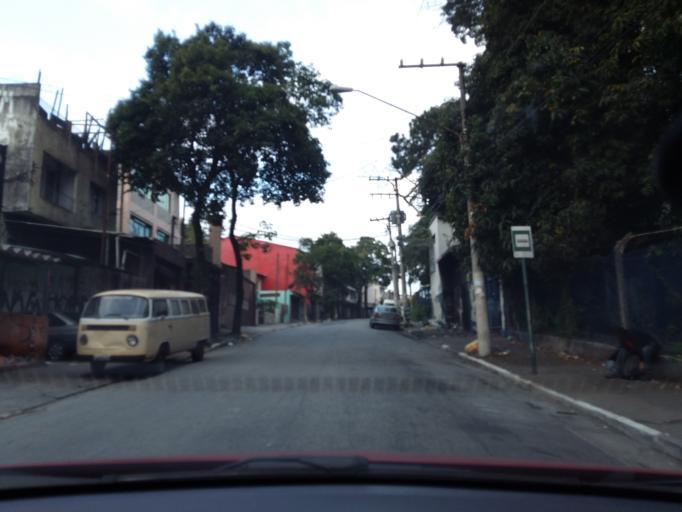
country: BR
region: Sao Paulo
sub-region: Sao Caetano Do Sul
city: Sao Caetano do Sul
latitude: -23.6367
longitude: -46.5933
